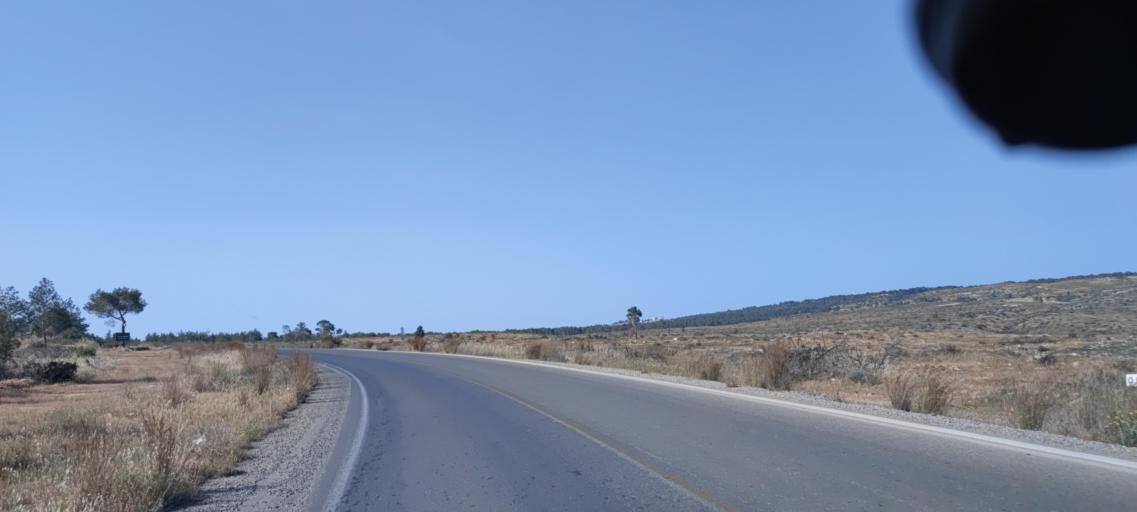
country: CY
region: Lefkosia
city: Morfou
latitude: 35.2771
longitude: 33.0414
